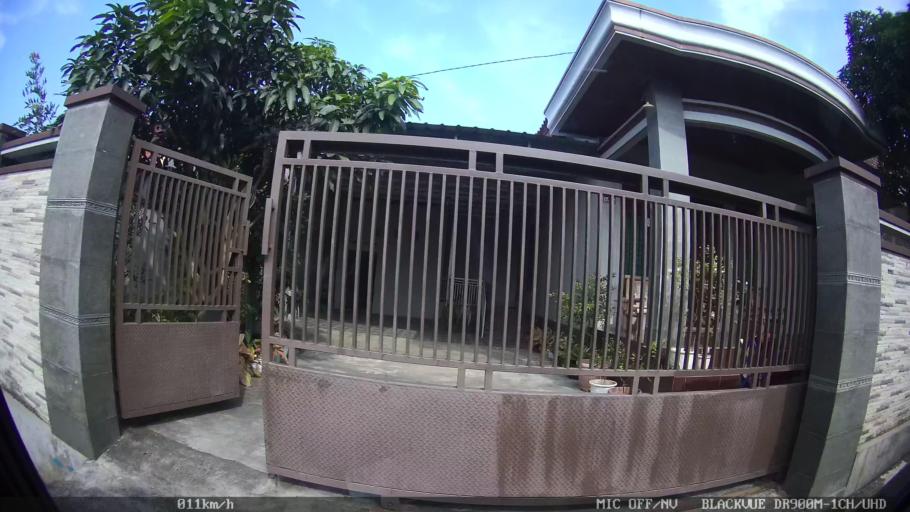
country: ID
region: Lampung
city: Kedaton
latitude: -5.3898
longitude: 105.2217
